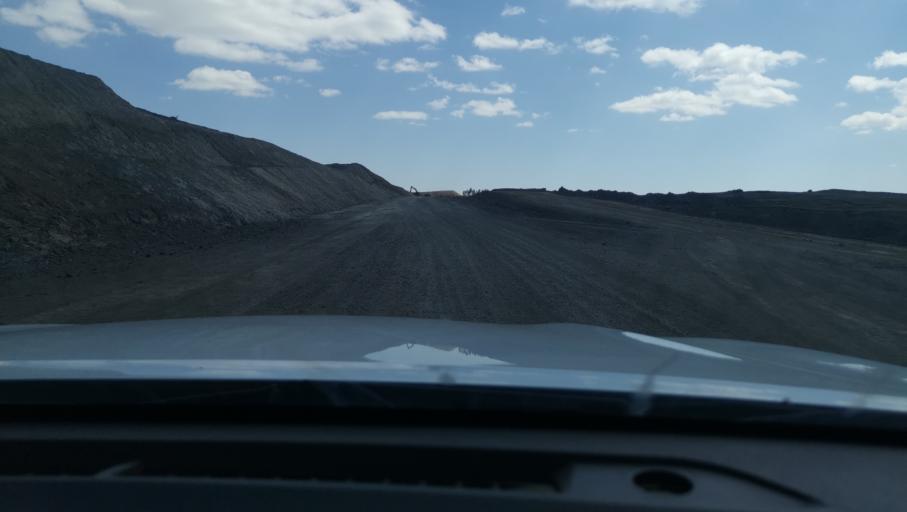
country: ET
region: Amhara
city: Debark'
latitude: 13.1556
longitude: 37.8438
